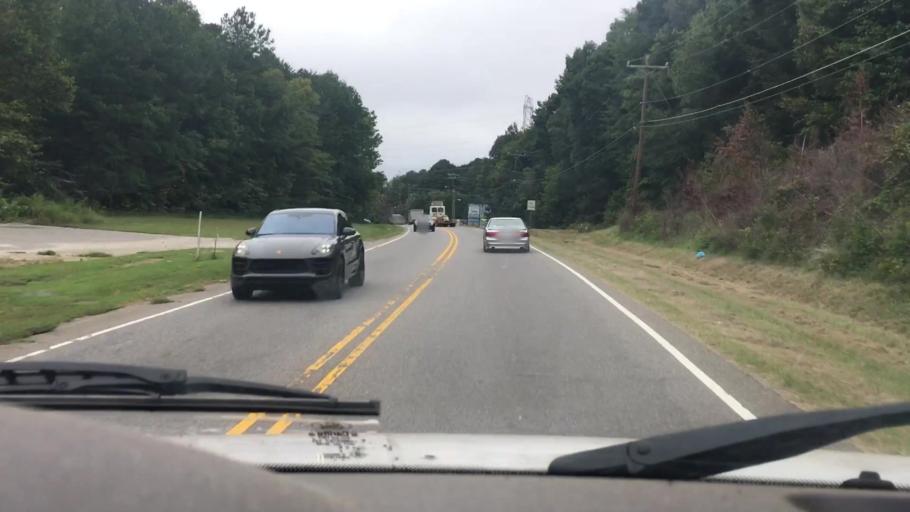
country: US
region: North Carolina
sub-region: Catawba County
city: Lake Norman of Catawba
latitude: 35.6058
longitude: -80.9323
